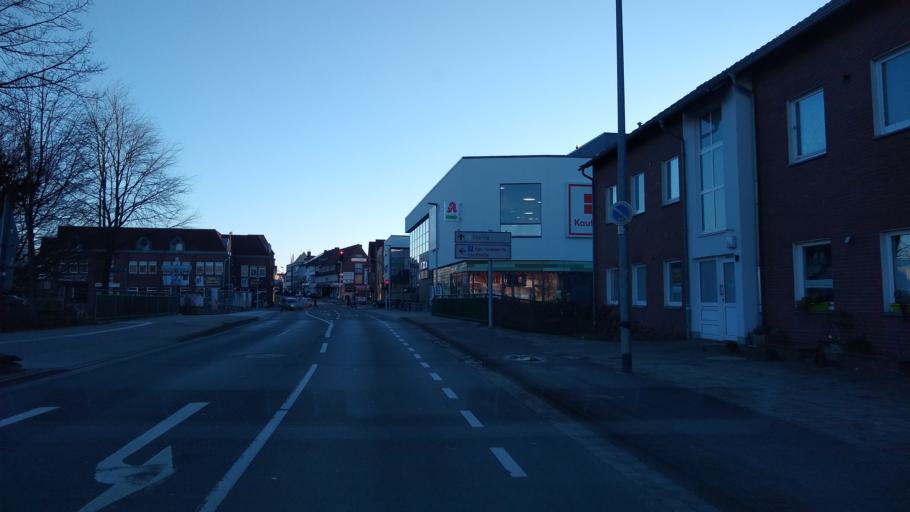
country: DE
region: Lower Saxony
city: Cloppenburg
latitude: 52.8461
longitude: 8.0365
